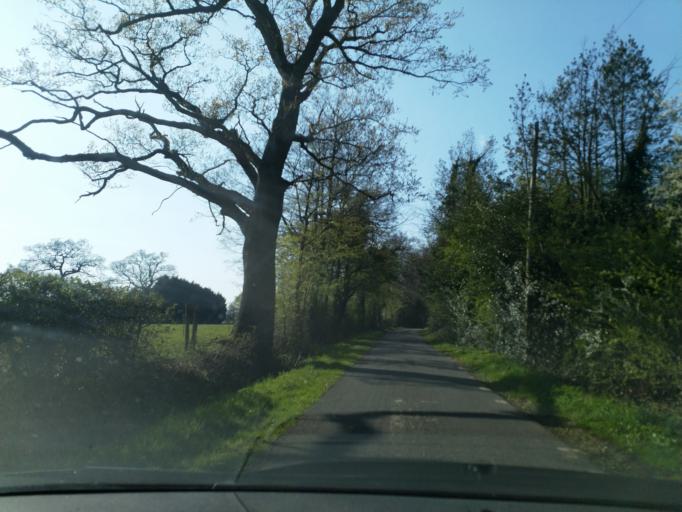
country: GB
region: England
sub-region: Warwickshire
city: Wroxall
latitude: 52.2860
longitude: -1.7091
